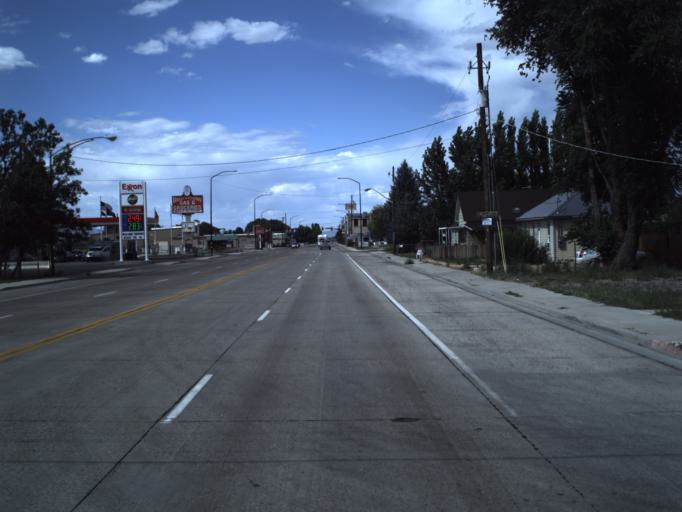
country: US
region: Utah
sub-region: Sevier County
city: Salina
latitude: 38.9549
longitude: -111.8600
